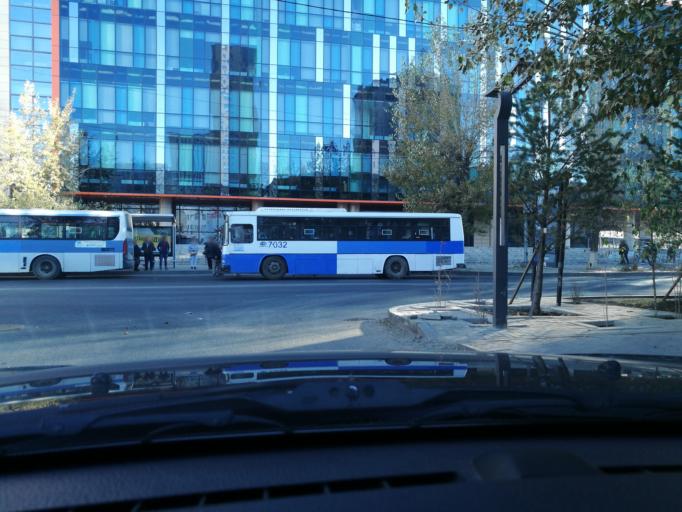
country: MN
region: Ulaanbaatar
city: Ulaanbaatar
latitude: 47.9222
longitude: 106.9204
